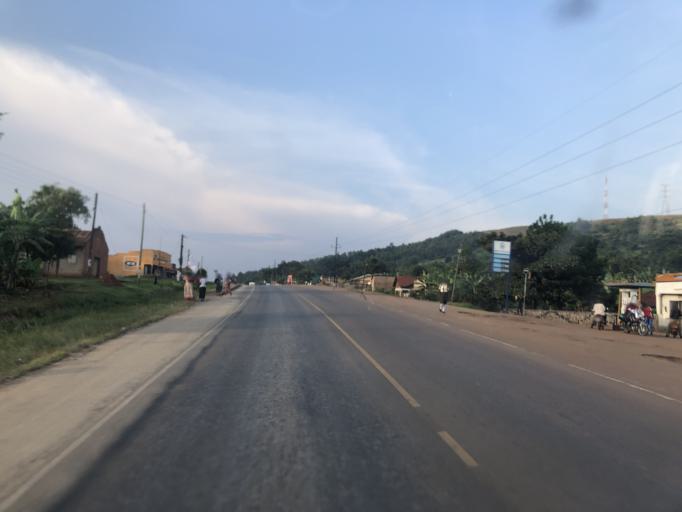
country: UG
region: Central Region
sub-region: Mpigi District
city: Mpigi
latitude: 0.1908
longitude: 32.2941
